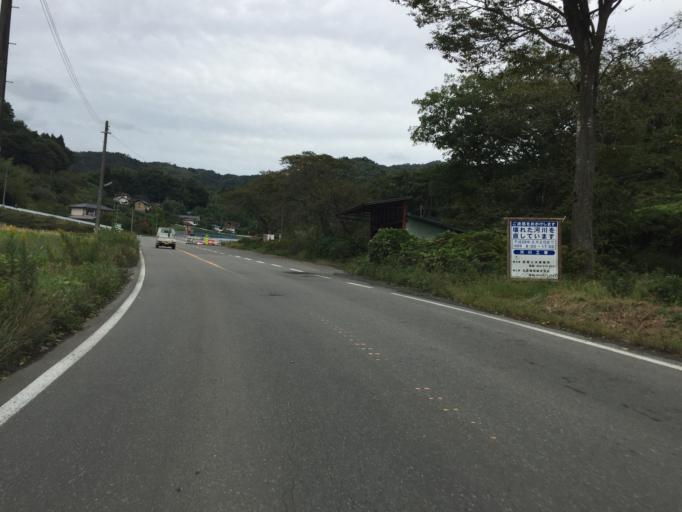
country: JP
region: Fukushima
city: Yanagawamachi-saiwaicho
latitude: 37.8764
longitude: 140.6487
